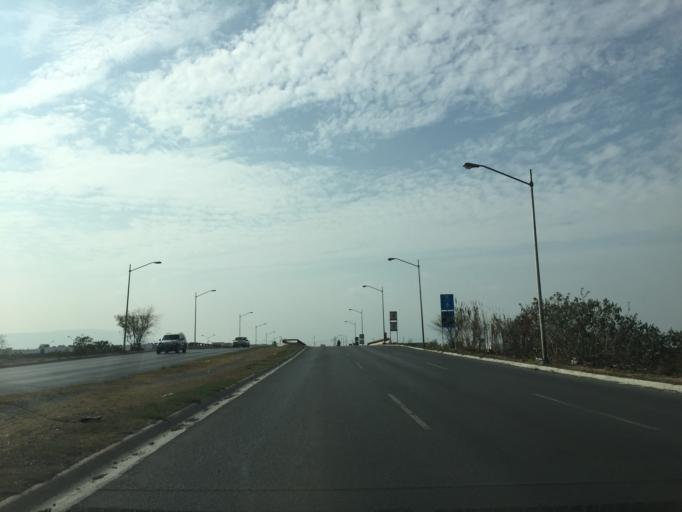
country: MX
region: Nuevo Leon
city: Apodaca
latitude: 25.7763
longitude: -100.2089
